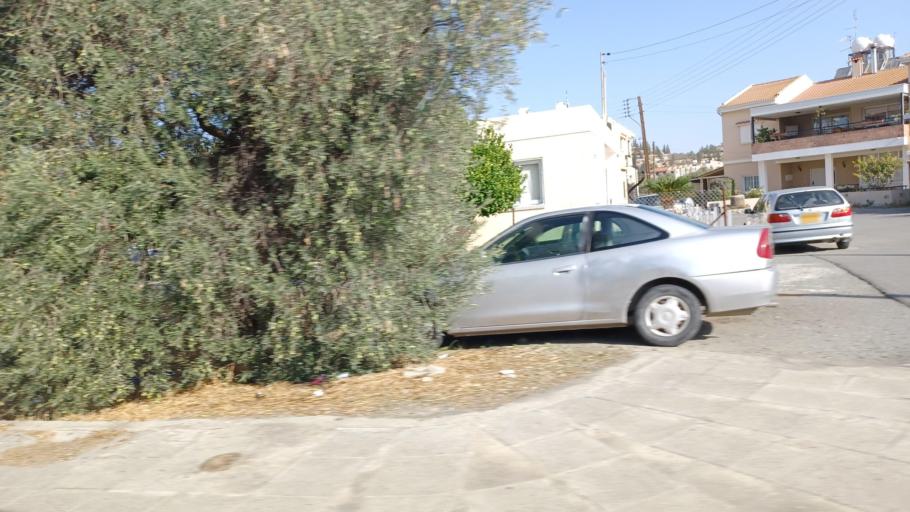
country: CY
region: Lefkosia
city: Alampra
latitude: 34.9994
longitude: 33.3718
